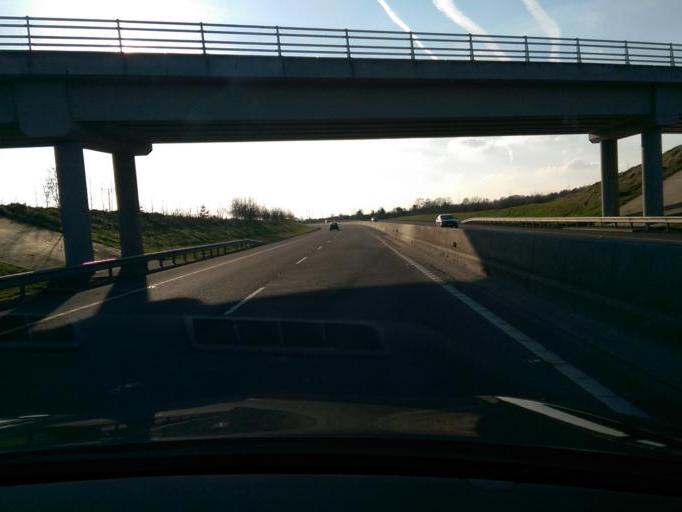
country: IE
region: Leinster
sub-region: Laois
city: Mountrath
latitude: 52.9952
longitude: -7.4115
